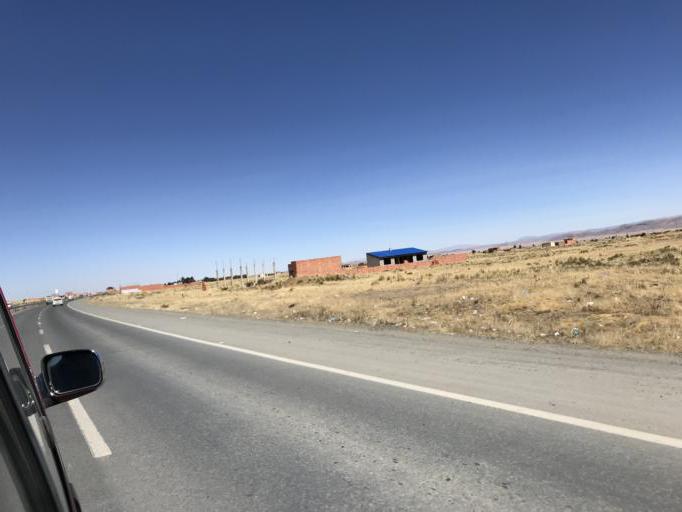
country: BO
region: La Paz
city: Batallas
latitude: -16.3408
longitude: -68.4106
